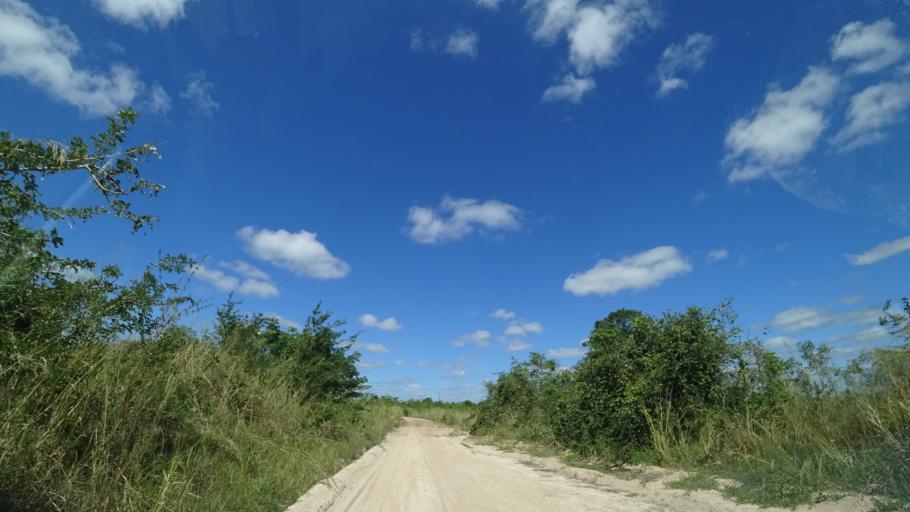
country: MZ
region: Sofala
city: Dondo
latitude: -19.2988
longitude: 34.6908
